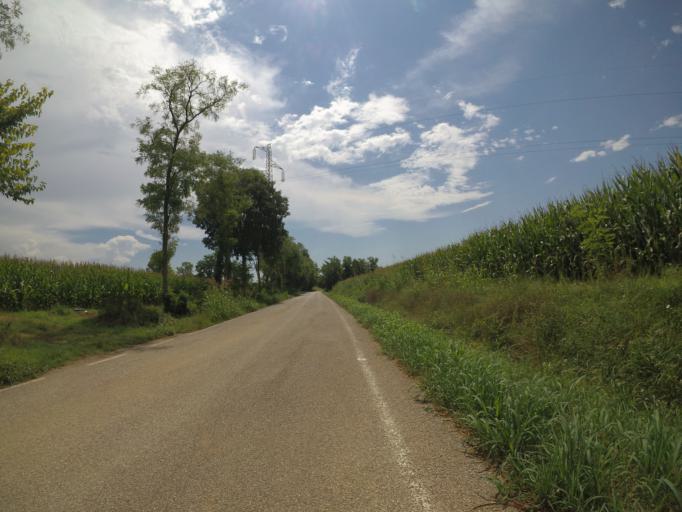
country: IT
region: Friuli Venezia Giulia
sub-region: Provincia di Udine
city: Talmassons
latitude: 45.9458
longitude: 13.0959
